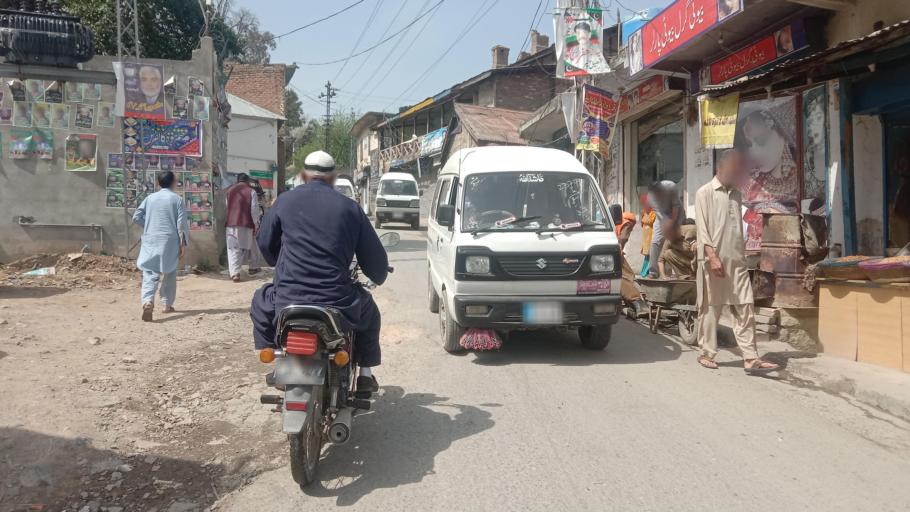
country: PK
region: Khyber Pakhtunkhwa
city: Abbottabad
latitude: 34.1473
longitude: 73.2036
